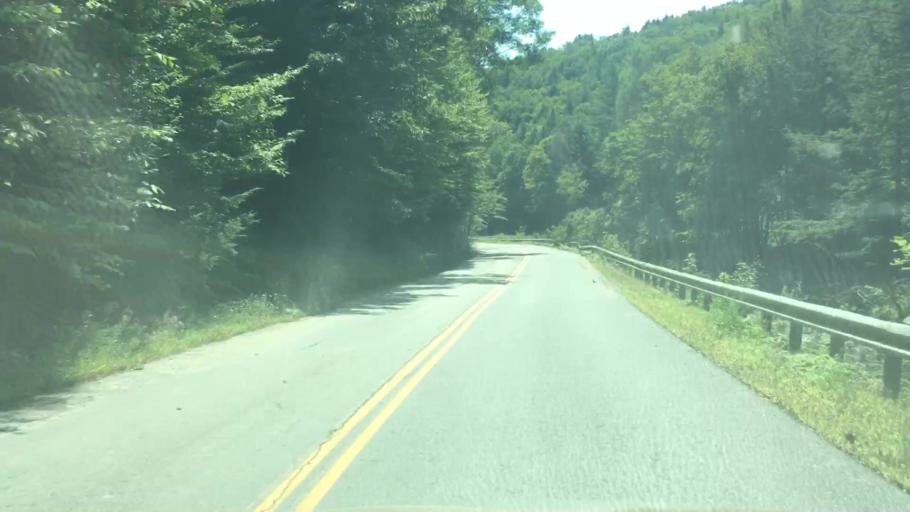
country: US
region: Vermont
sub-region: Windham County
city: West Brattleboro
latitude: 42.7994
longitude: -72.6843
